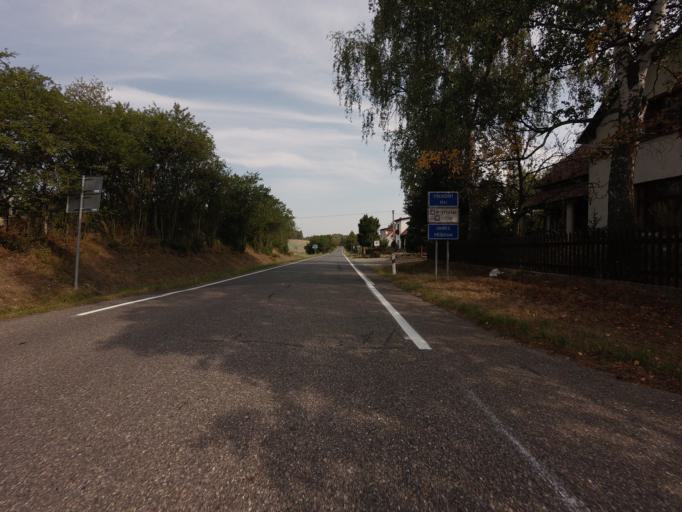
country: CZ
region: Central Bohemia
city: Petrovice
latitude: 49.5245
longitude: 14.3546
